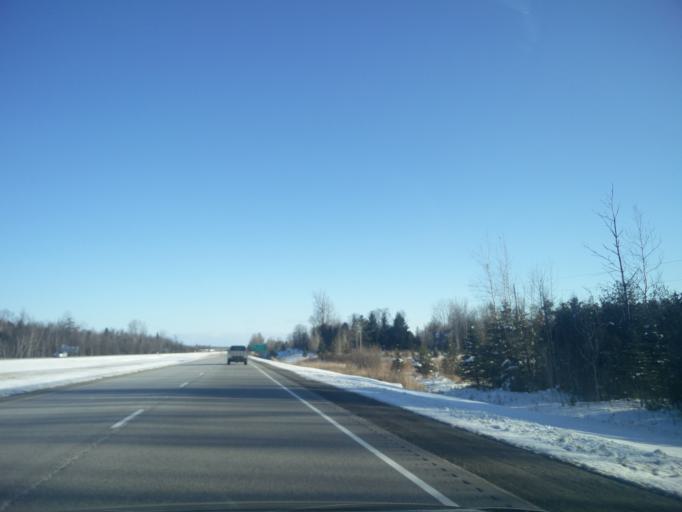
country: CA
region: Ontario
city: Prescott
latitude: 44.9621
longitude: -75.5960
